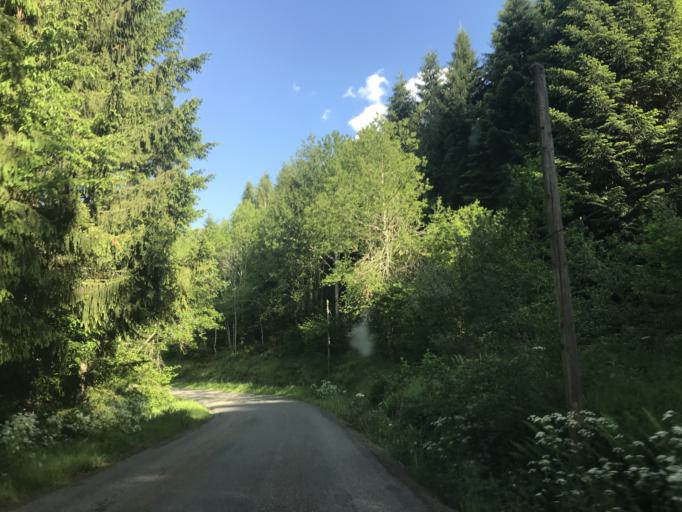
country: FR
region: Auvergne
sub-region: Departement du Puy-de-Dome
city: Job
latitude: 45.6102
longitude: 3.6643
